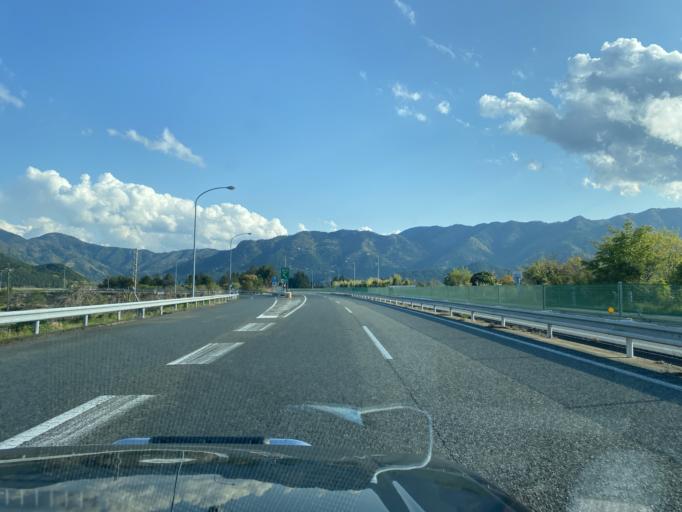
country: JP
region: Kyoto
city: Fukuchiyama
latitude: 35.1680
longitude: 135.1191
